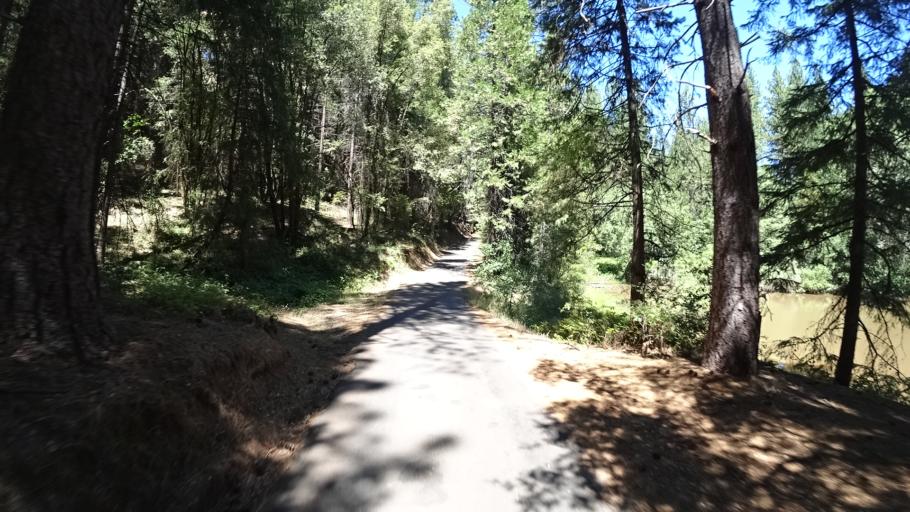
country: US
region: California
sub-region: Amador County
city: Pioneer
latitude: 38.3562
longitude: -120.5589
